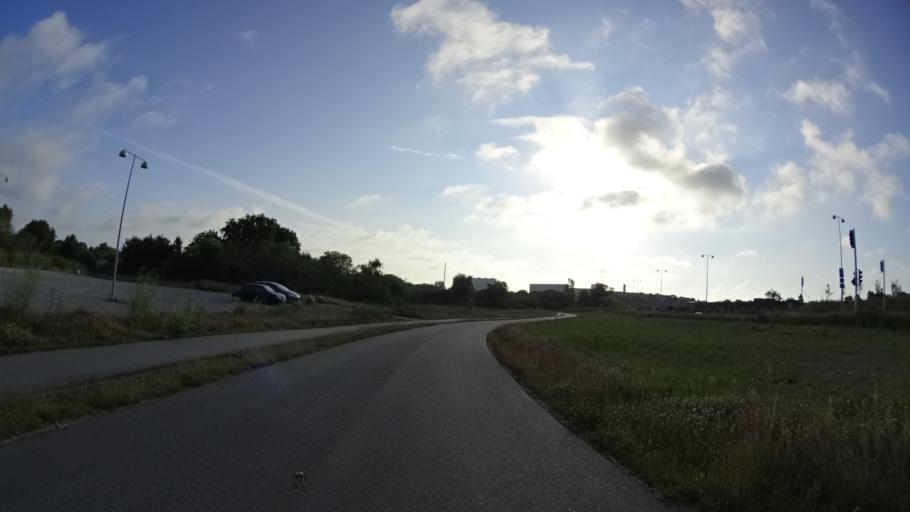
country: DK
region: Central Jutland
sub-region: Arhus Kommune
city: Arhus
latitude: 56.1397
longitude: 10.1683
